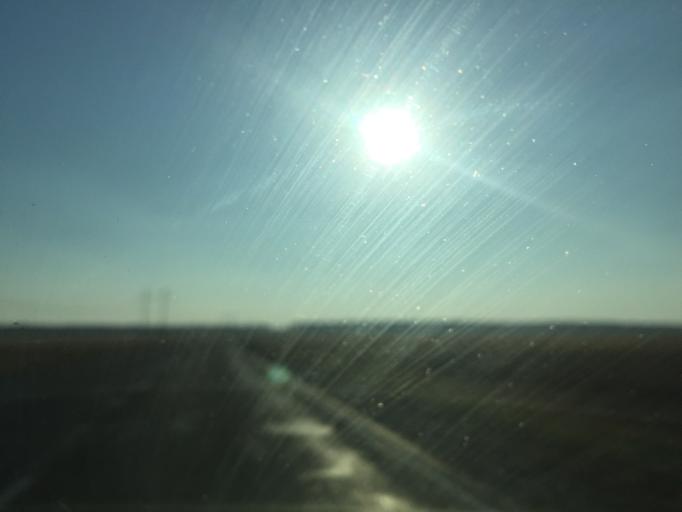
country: BY
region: Gomel
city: Dobrush
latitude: 52.3768
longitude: 31.2610
